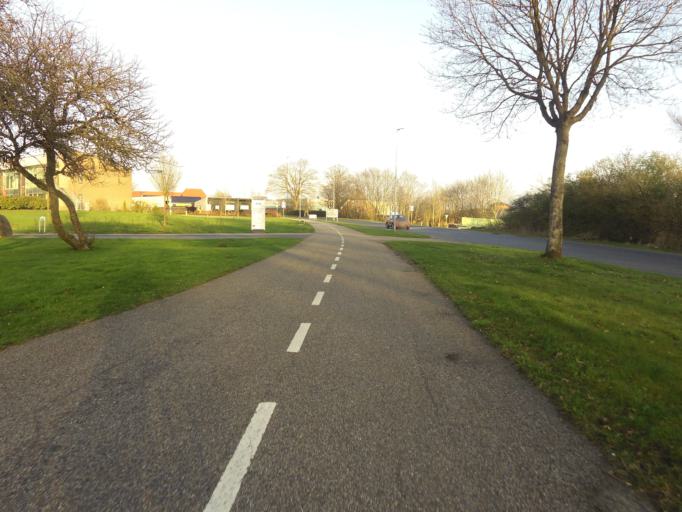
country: DK
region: South Denmark
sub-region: Vejen Kommune
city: Vejen
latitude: 55.4783
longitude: 9.1300
